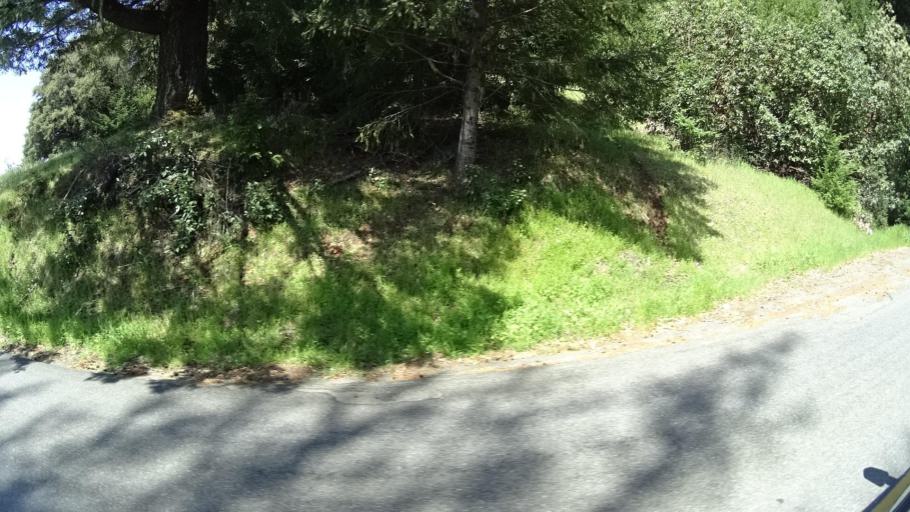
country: US
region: California
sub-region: Humboldt County
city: Redway
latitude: 40.0918
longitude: -123.6778
